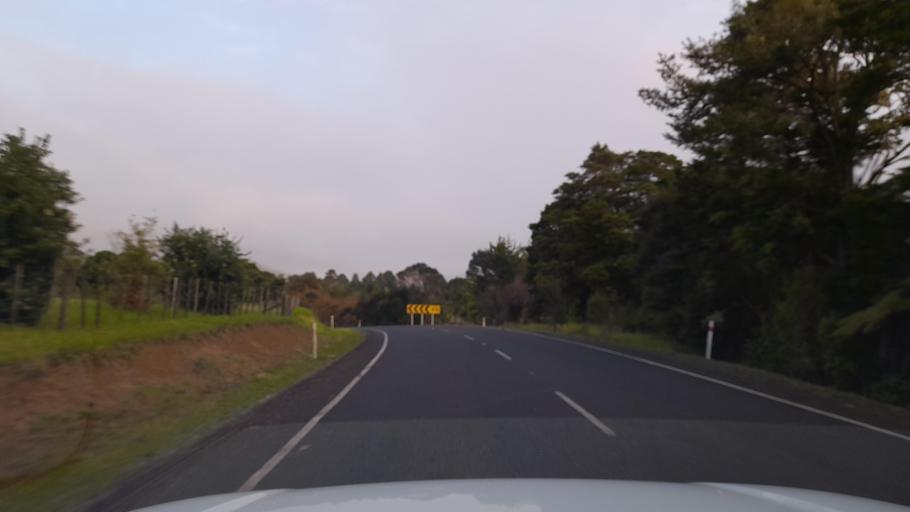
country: NZ
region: Northland
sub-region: Kaipara District
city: Dargaville
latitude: -35.6411
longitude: 173.8564
